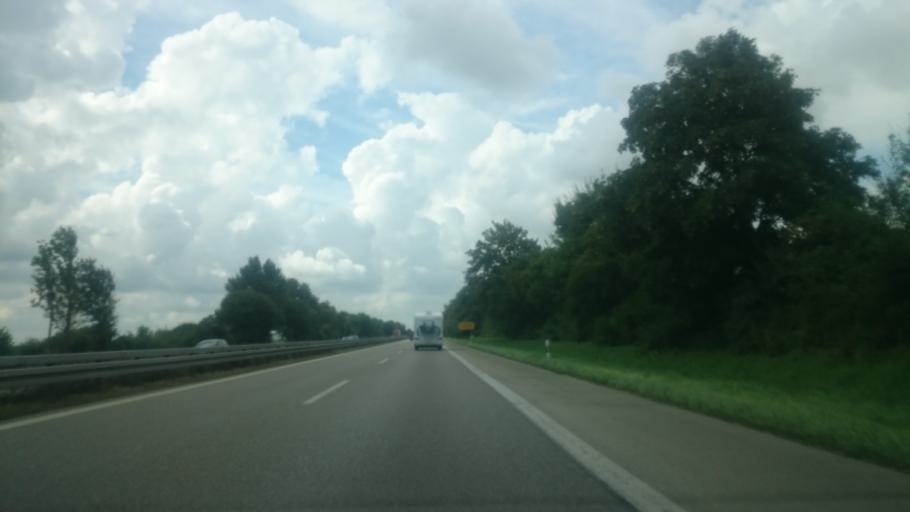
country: DE
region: Bavaria
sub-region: Swabia
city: Oberottmarshausen
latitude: 48.2147
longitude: 10.8609
